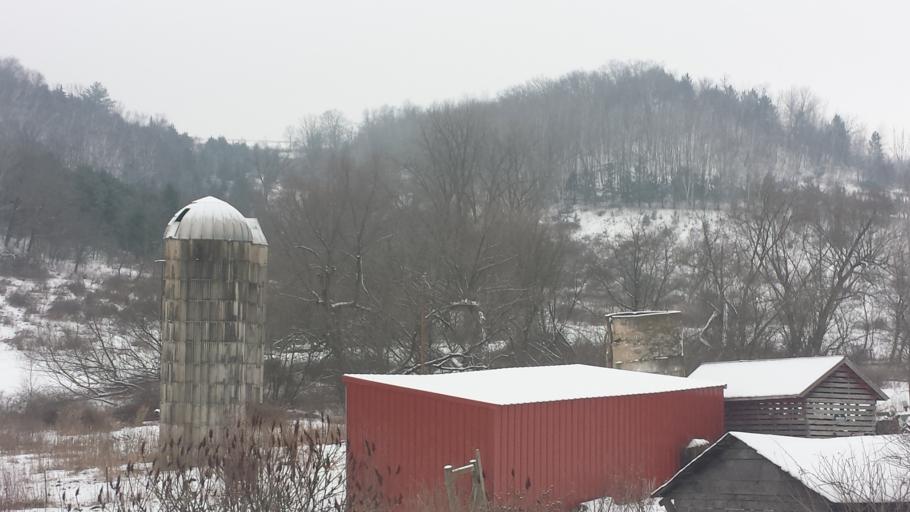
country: US
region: Wisconsin
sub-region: Monroe County
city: Cashton
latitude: 43.7201
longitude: -90.6769
